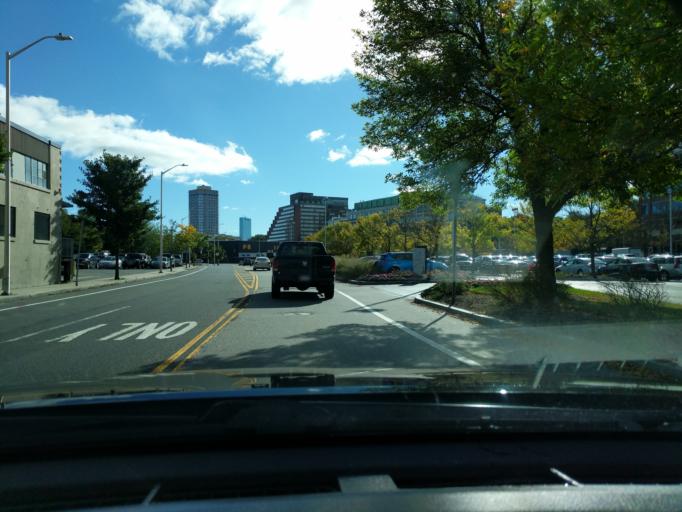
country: US
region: Massachusetts
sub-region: Middlesex County
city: Cambridge
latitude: 42.3550
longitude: -71.1097
